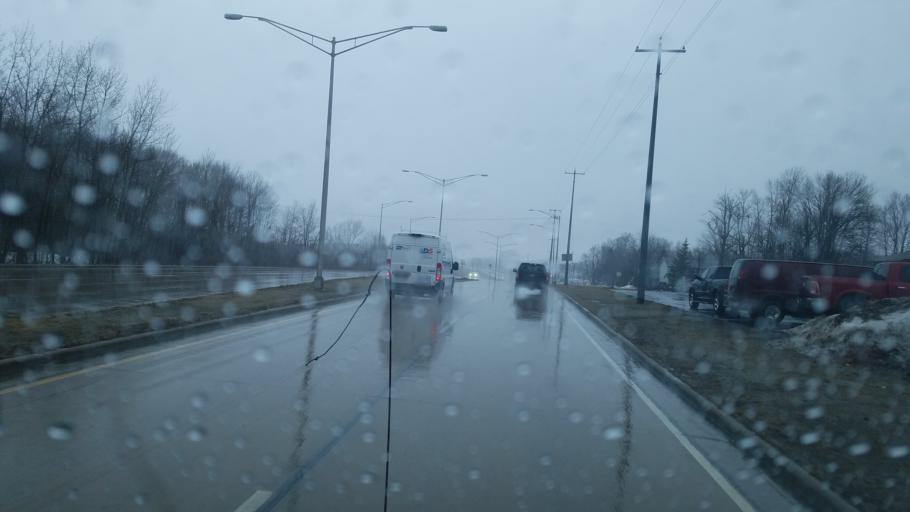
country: US
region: Wisconsin
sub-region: Wood County
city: Marshfield
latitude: 44.6757
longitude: -90.1886
